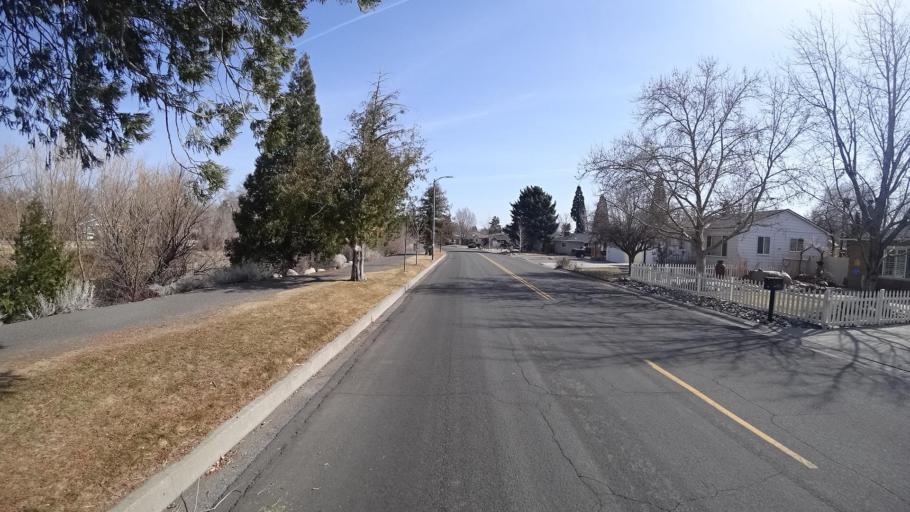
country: US
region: Nevada
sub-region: Washoe County
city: Reno
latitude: 39.5182
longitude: -119.8404
